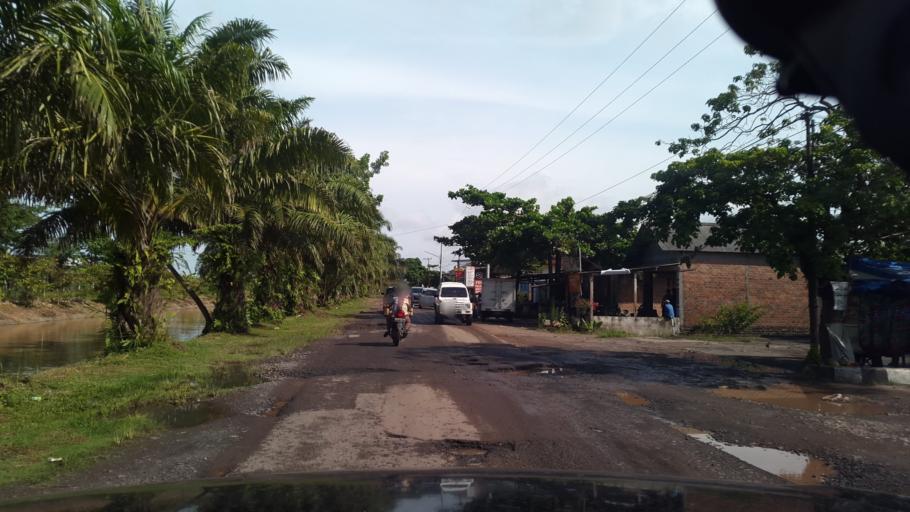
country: ID
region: South Sumatra
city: Gumawang
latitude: -4.1352
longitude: 104.6279
